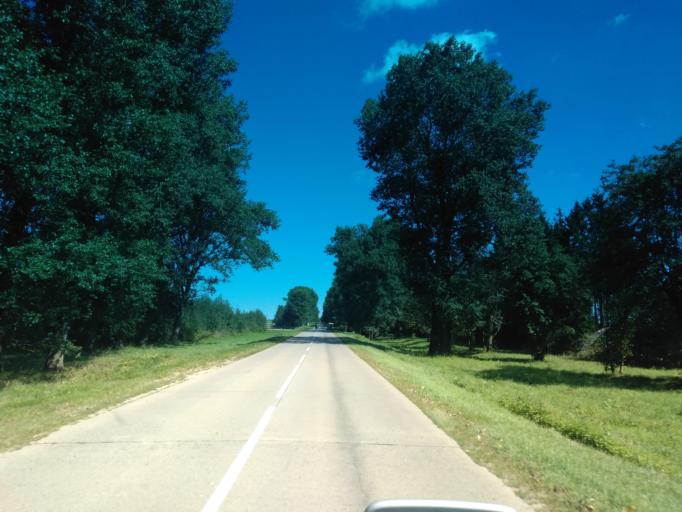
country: BY
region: Minsk
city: Stan'kava
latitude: 53.6552
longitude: 27.3158
